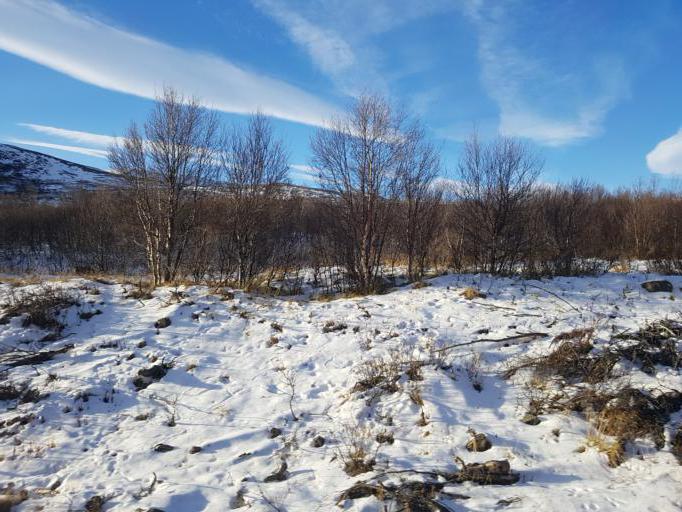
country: NO
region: Oppland
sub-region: Dovre
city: Dovre
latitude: 62.2250
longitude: 9.5374
